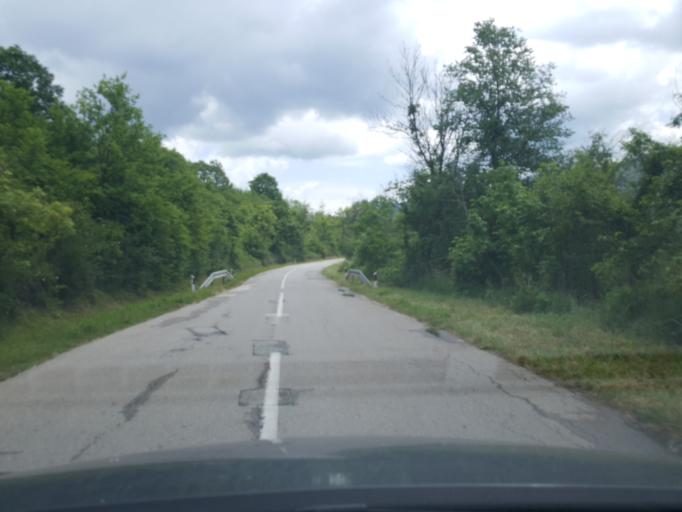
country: RS
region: Central Serbia
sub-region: Zajecarski Okrug
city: Soko Banja
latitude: 43.6465
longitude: 21.9311
